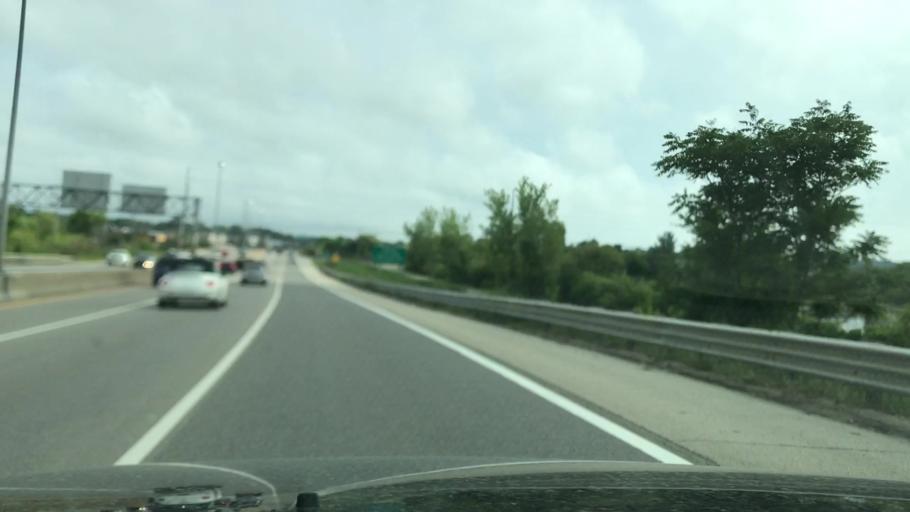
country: US
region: Michigan
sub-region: Ottawa County
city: Ferrysburg
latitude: 43.0730
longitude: -86.2193
